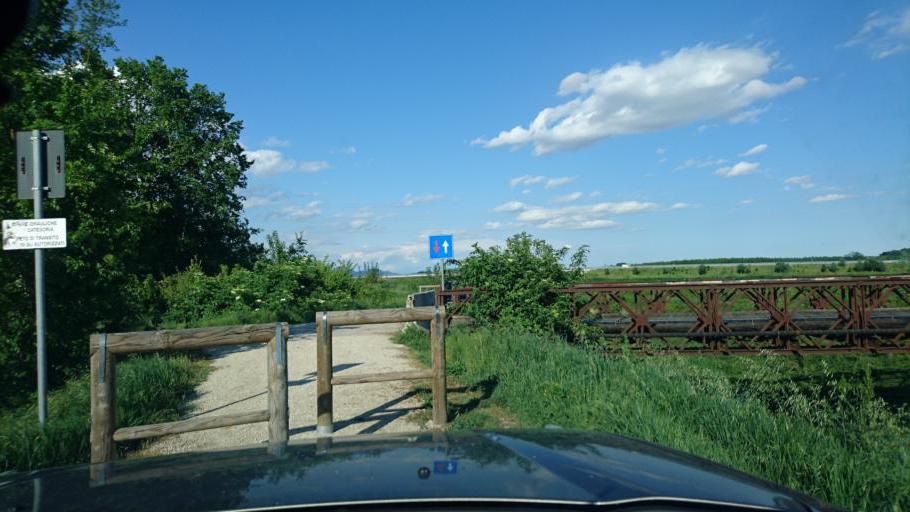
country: IT
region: Veneto
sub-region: Provincia di Padova
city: Piacenza d'Adige
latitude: 45.1523
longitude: 11.5280
